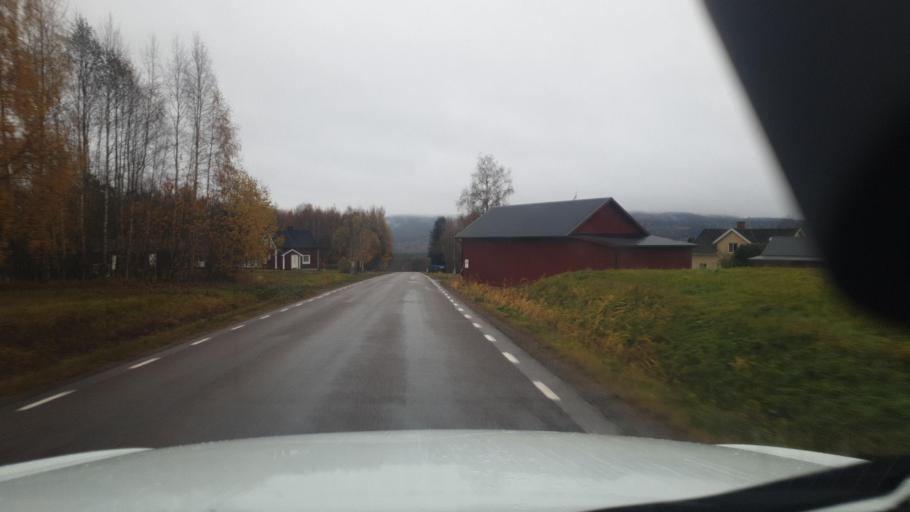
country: SE
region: Vaermland
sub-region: Torsby Kommun
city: Torsby
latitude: 59.9213
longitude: 12.8898
